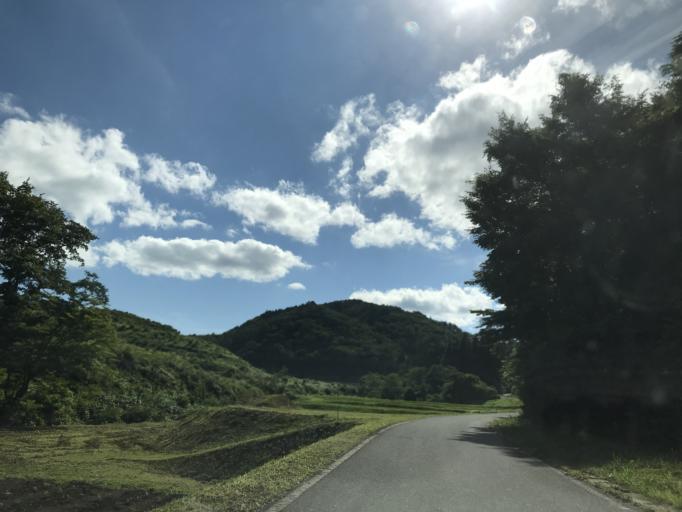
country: JP
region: Iwate
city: Ichinoseki
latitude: 38.9212
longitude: 140.9649
